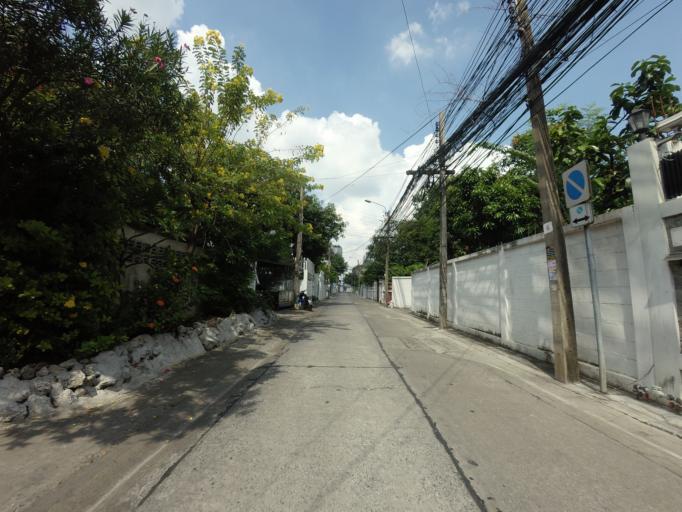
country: TH
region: Bangkok
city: Phaya Thai
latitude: 13.7843
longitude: 100.5520
